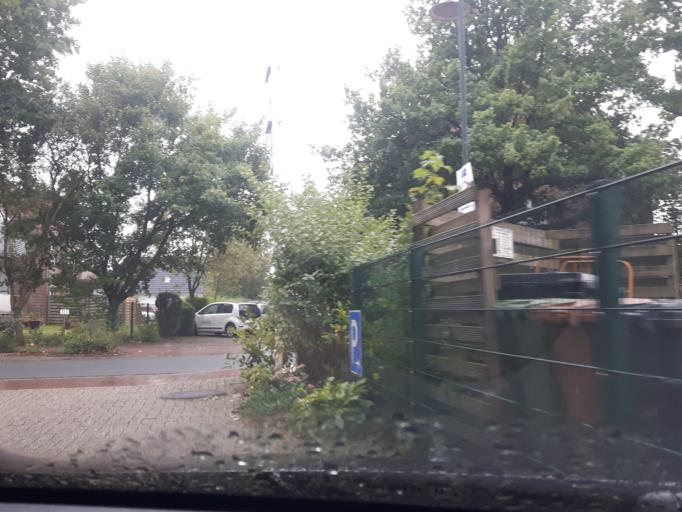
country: DE
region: Lower Saxony
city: Grossenkneten
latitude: 52.9905
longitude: 8.2762
